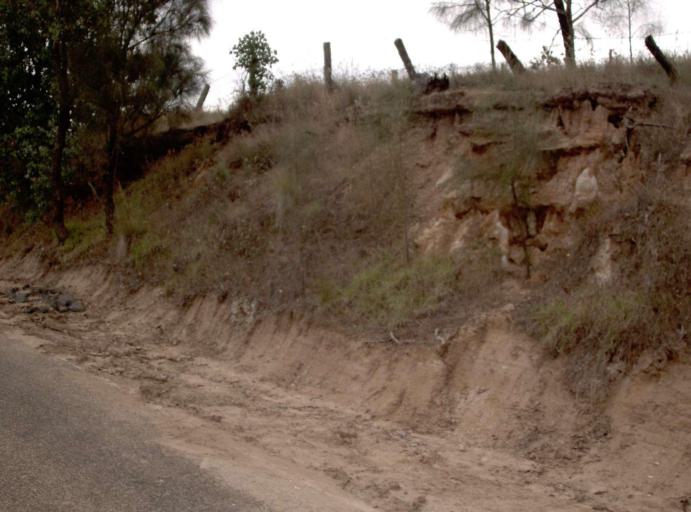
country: AU
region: Victoria
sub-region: Wellington
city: Sale
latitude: -38.0111
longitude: 147.1892
